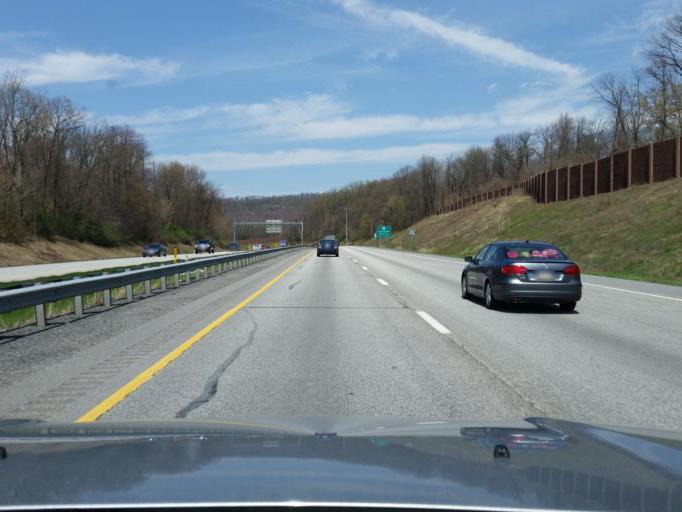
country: US
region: Pennsylvania
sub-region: Dauphin County
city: Harrisburg
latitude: 40.3166
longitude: -76.8824
